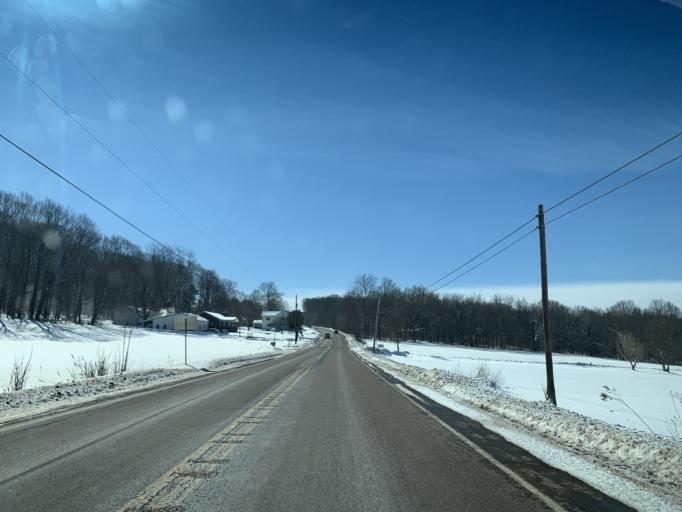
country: US
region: Pennsylvania
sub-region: Somerset County
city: Meyersdale
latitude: 39.7308
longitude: -79.0863
